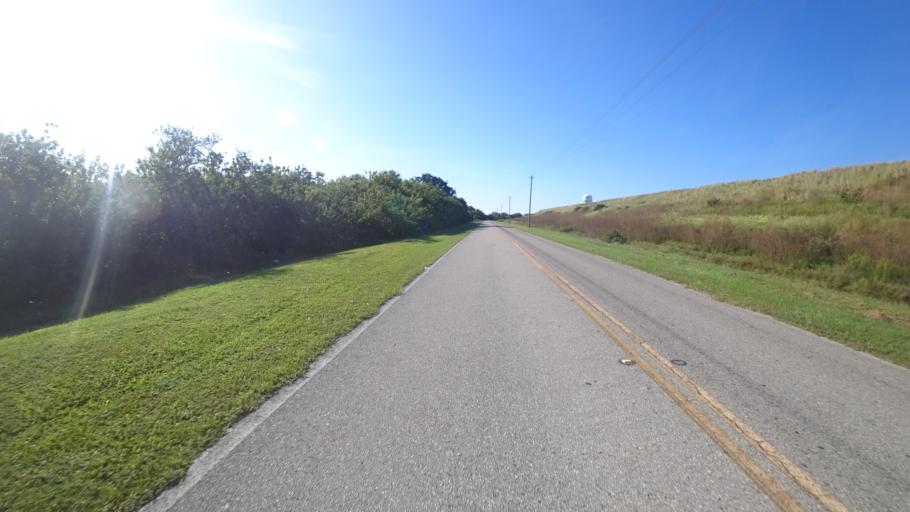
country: US
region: Florida
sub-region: Manatee County
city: Memphis
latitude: 27.6407
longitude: -82.5399
